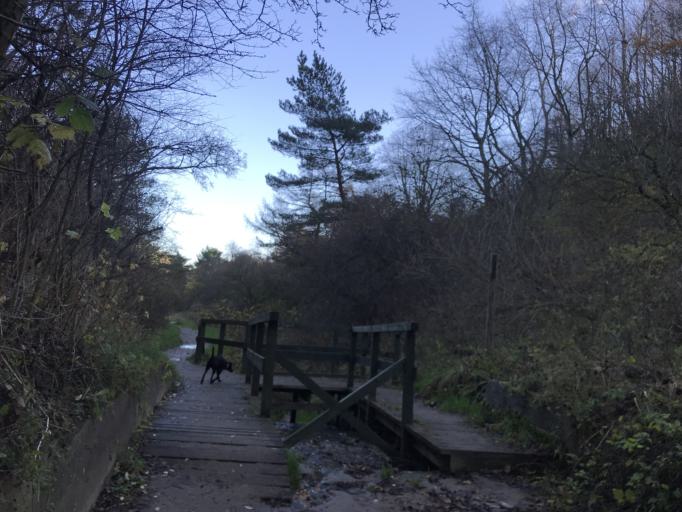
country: PL
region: Pomeranian Voivodeship
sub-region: Powiat pucki
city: Chlapowo
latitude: 54.8102
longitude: 18.3660
